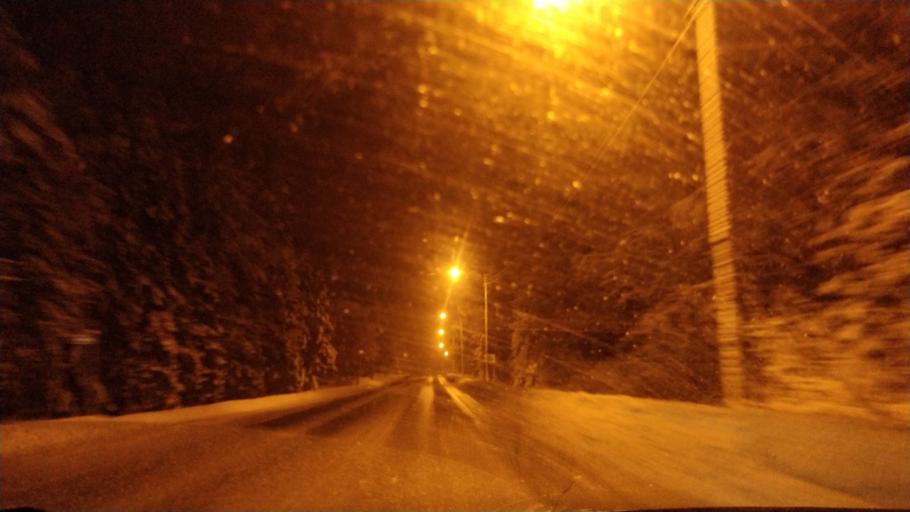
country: FI
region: Lapland
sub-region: Rovaniemi
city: Rovaniemi
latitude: 66.4177
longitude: 25.4145
